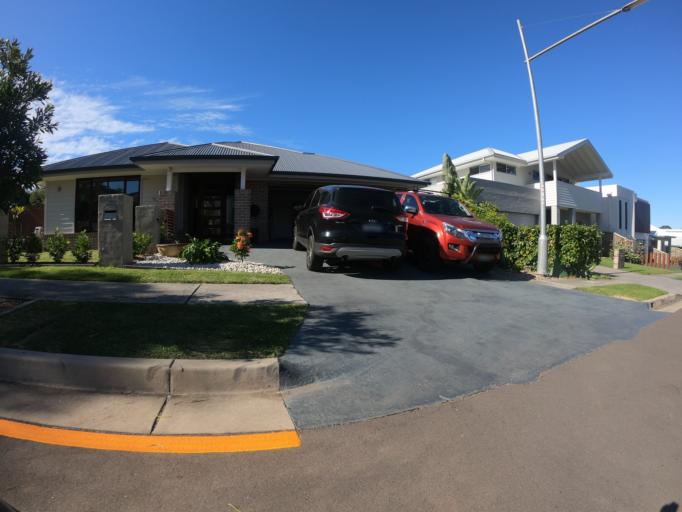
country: AU
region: New South Wales
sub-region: Wollongong
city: Bulli
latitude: -34.3210
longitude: 150.9200
